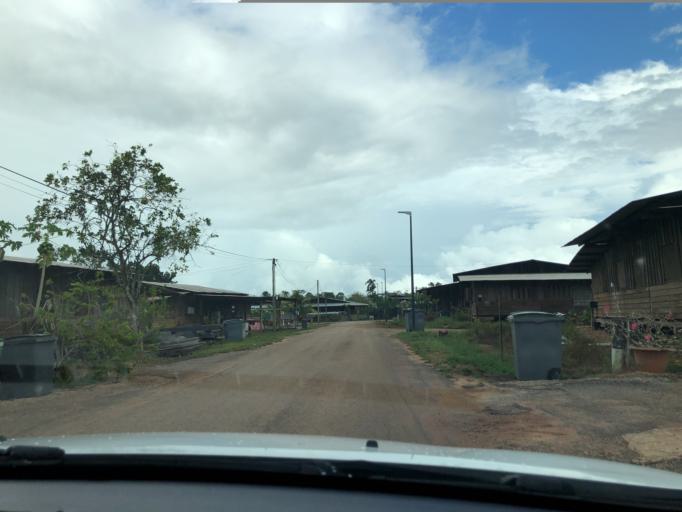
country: GF
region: Guyane
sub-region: Guyane
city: Mana
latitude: 5.6077
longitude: -53.8205
